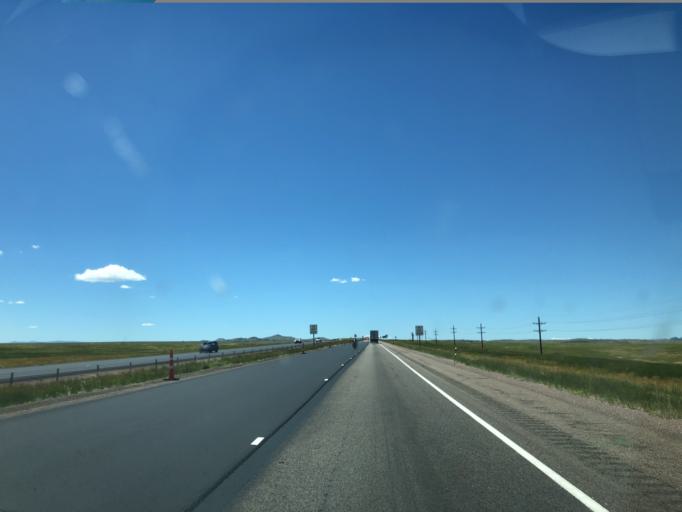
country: US
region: Wyoming
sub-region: Laramie County
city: Cheyenne
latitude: 41.1002
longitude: -105.0816
